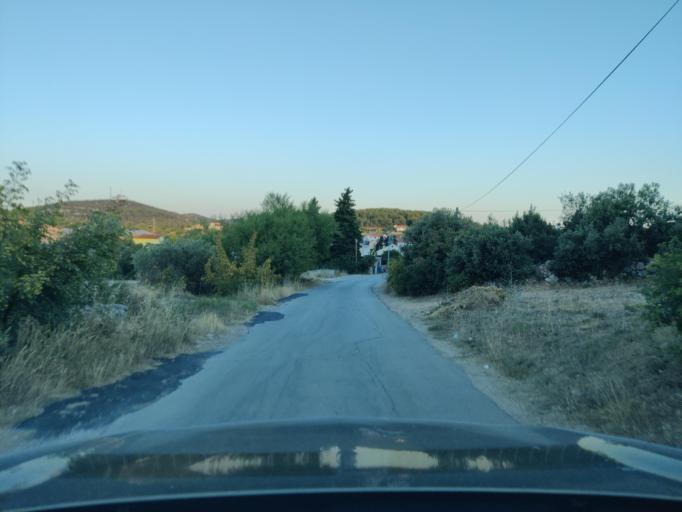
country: HR
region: Sibensko-Kniniska
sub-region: Grad Sibenik
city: Tisno
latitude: 43.8047
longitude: 15.6472
